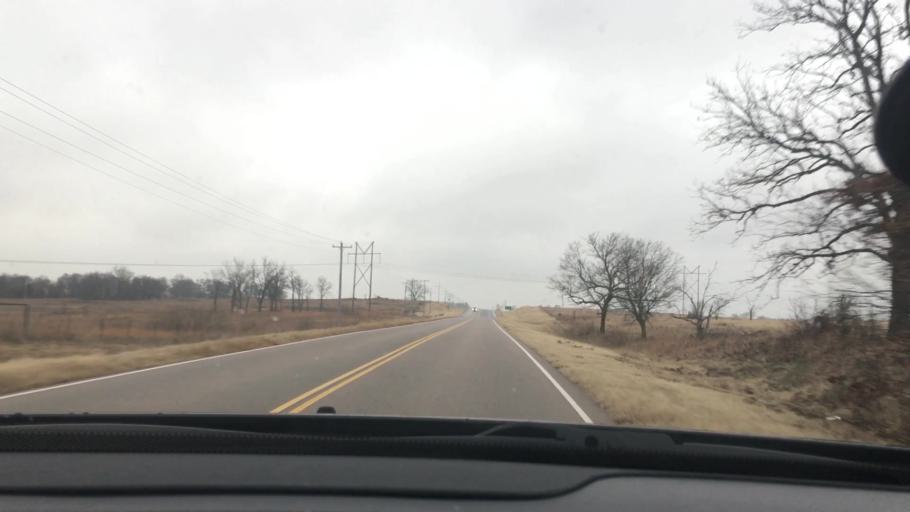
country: US
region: Oklahoma
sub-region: Johnston County
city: Tishomingo
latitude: 34.3697
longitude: -96.6360
